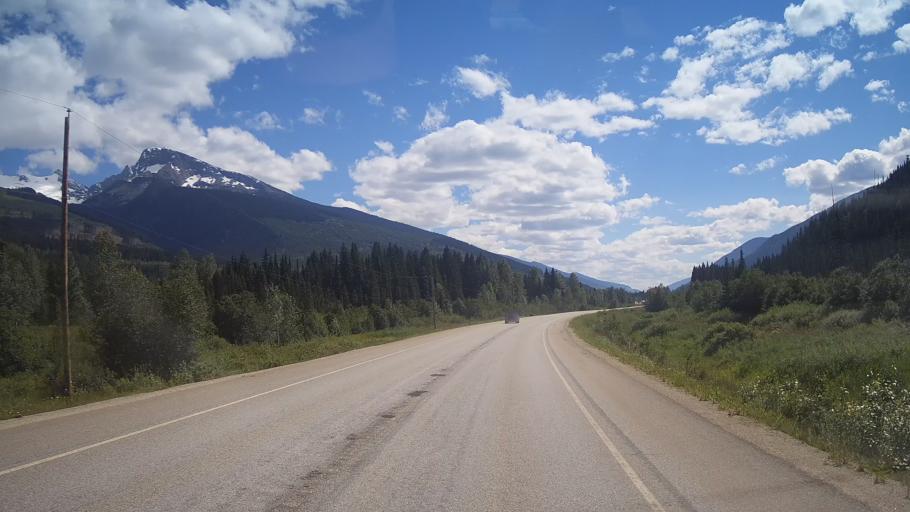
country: CA
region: Alberta
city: Jasper Park Lodge
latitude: 52.5834
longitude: -119.0953
